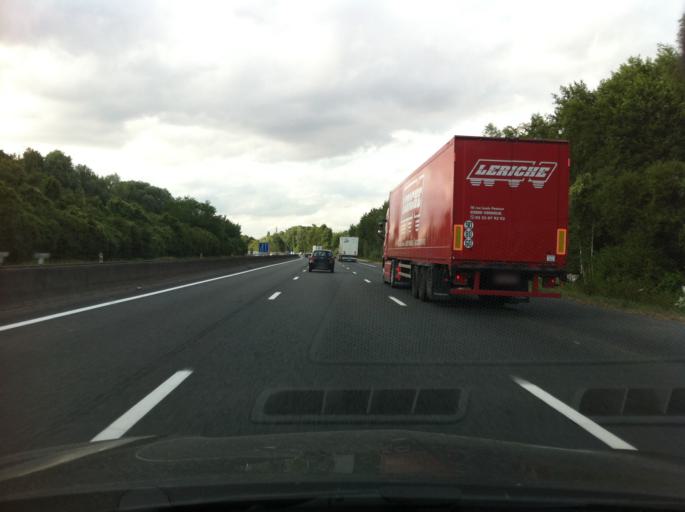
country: FR
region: Ile-de-France
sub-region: Departement de Seine-et-Marne
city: Pomponne
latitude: 48.8878
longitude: 2.6678
